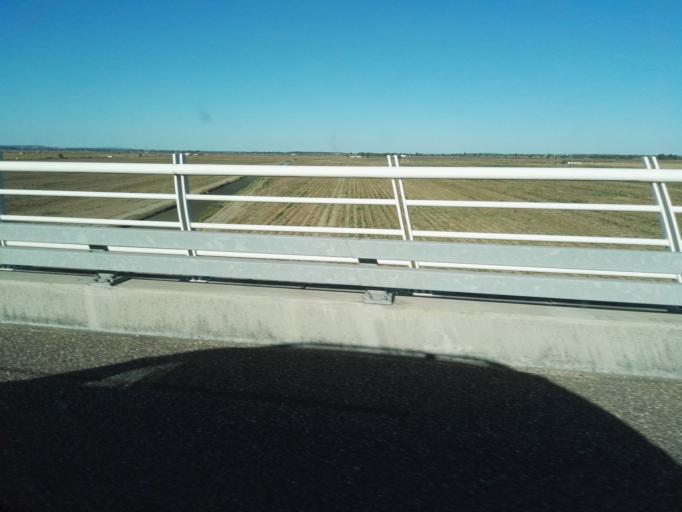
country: PT
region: Santarem
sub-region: Benavente
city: Samora Correia
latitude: 38.9814
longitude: -8.8854
